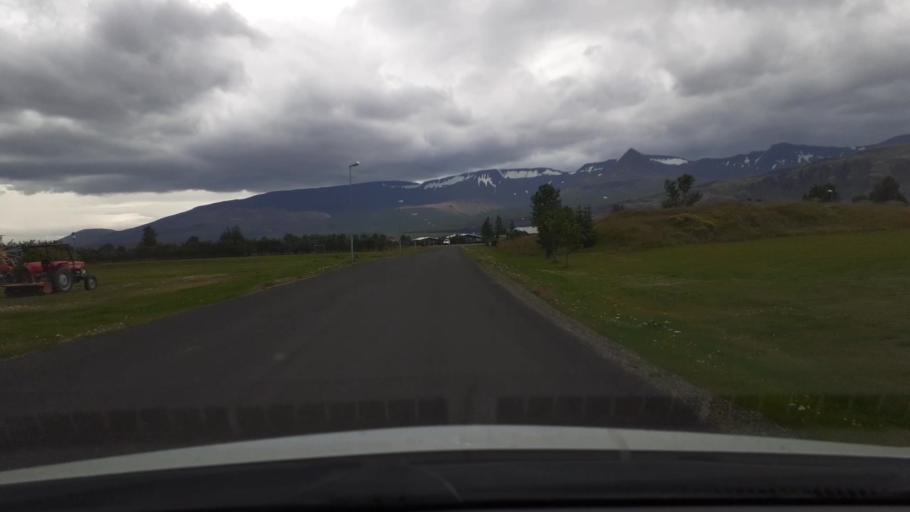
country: IS
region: West
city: Borgarnes
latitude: 64.5649
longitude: -21.7629
